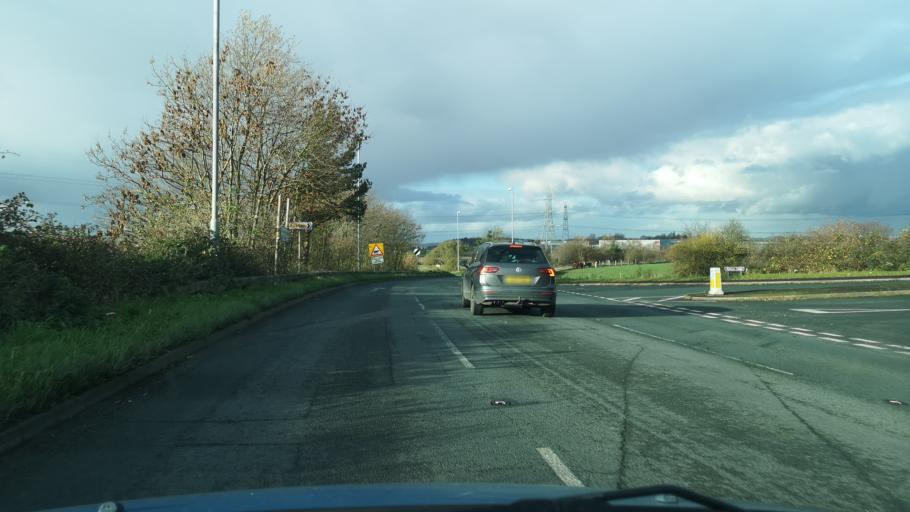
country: GB
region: England
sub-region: City and Borough of Wakefield
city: Featherstone
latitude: 53.6904
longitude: -1.3798
